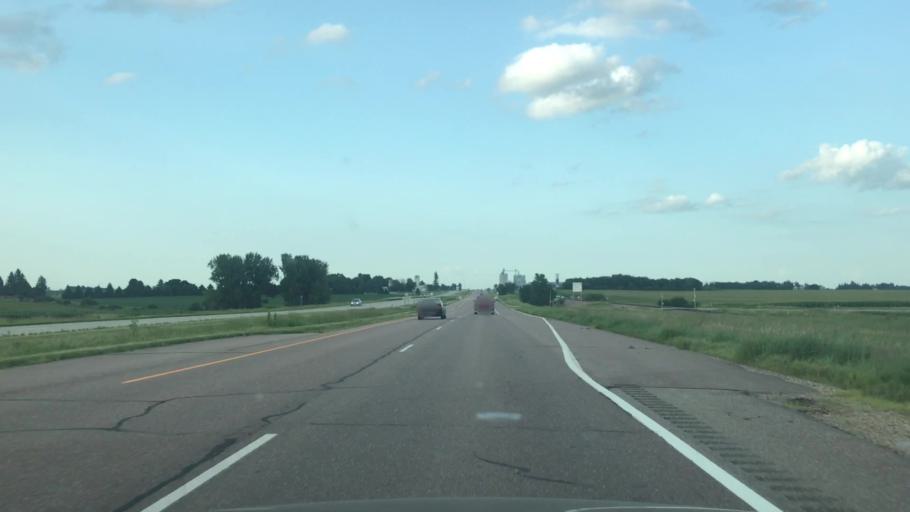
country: US
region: Minnesota
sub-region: Nobles County
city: Worthington
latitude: 43.6831
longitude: -95.4953
